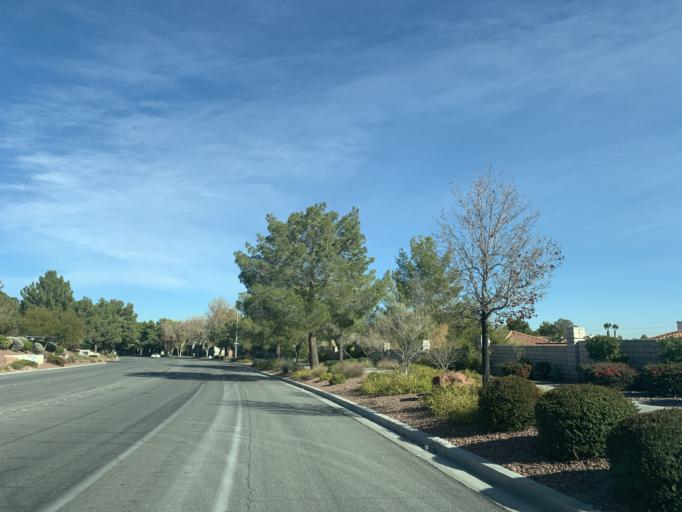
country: US
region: Nevada
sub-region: Clark County
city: Spring Valley
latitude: 36.1342
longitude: -115.2837
